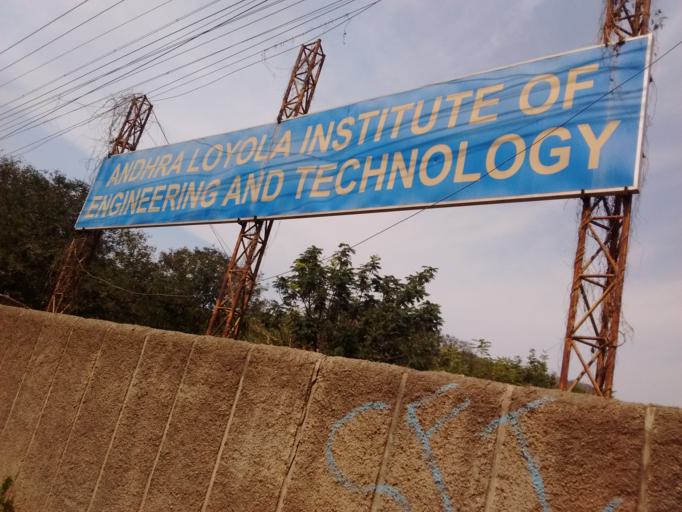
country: IN
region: Andhra Pradesh
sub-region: Krishna
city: Yanamalakuduru
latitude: 16.5062
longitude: 80.6582
